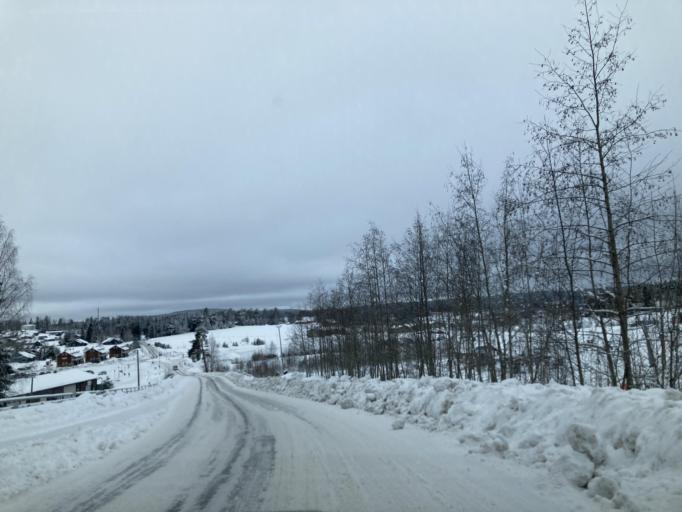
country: FI
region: Central Finland
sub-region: Jaemsae
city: Jaemsae
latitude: 61.8803
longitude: 25.3062
